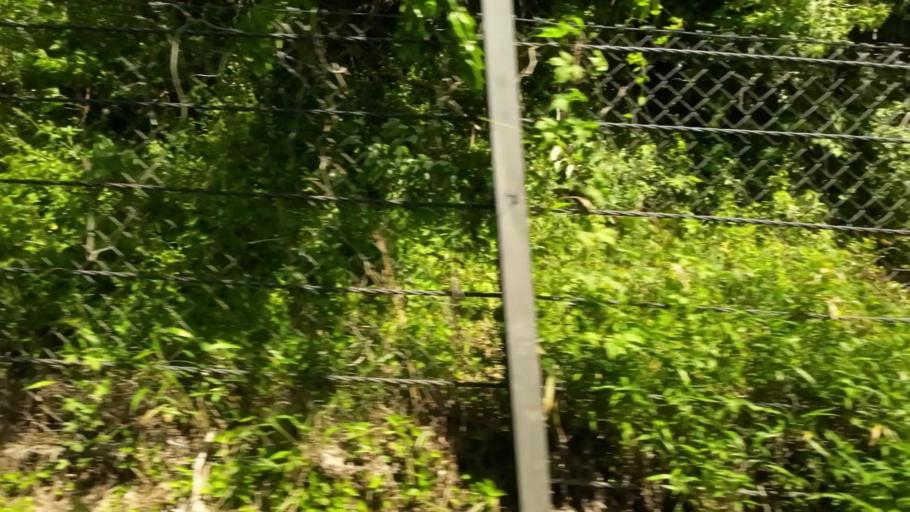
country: JP
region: Tokushima
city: Ikedacho
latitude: 34.0291
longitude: 133.8001
